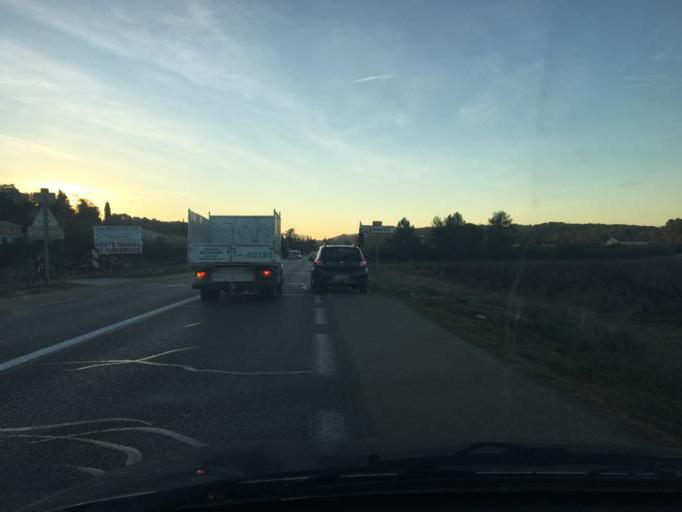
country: FR
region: Provence-Alpes-Cote d'Azur
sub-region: Departement du Var
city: Lorgues
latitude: 43.4850
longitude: 6.3675
